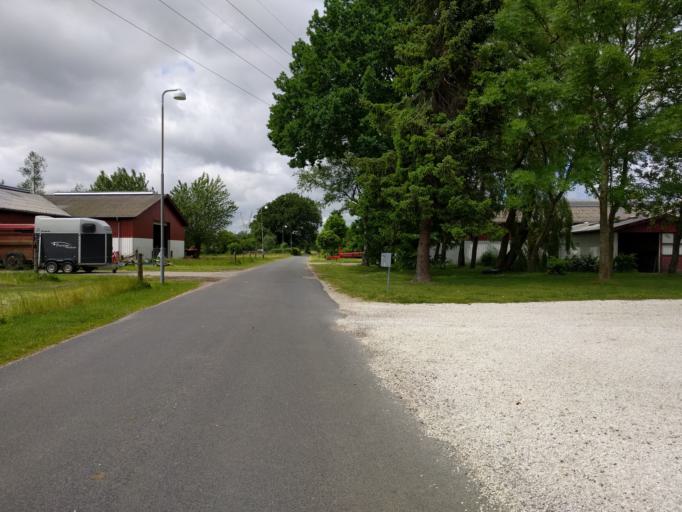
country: DK
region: South Denmark
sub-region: Odense Kommune
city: Bullerup
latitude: 55.4234
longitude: 10.5077
